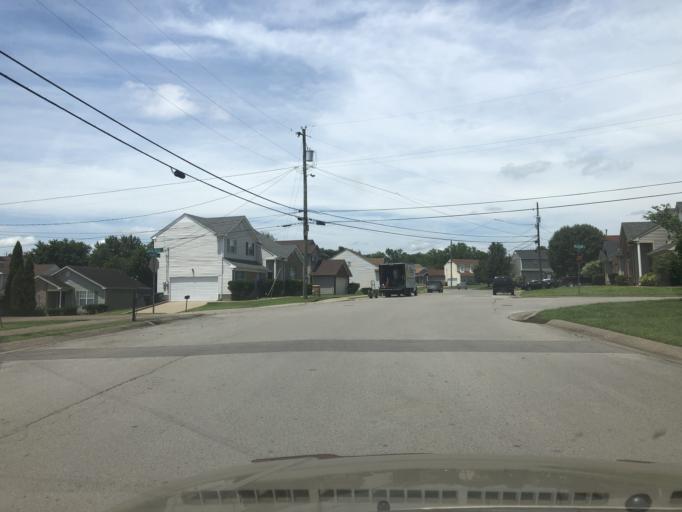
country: US
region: Tennessee
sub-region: Davidson County
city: Lakewood
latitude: 36.2520
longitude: -86.6725
